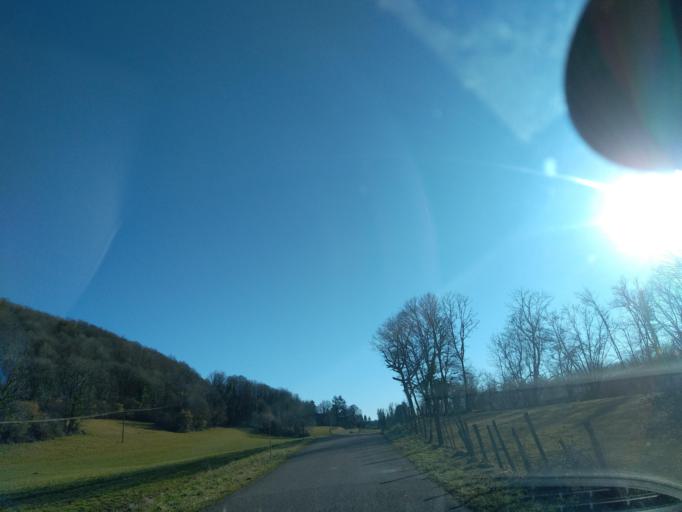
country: FR
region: Franche-Comte
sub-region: Departement du Jura
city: Clairvaux-les-Lacs
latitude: 46.7052
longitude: 5.7342
